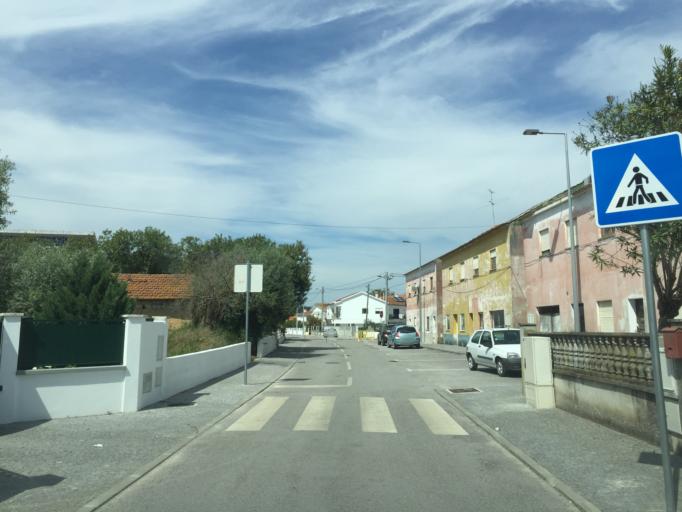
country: PT
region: Coimbra
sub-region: Soure
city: Soure
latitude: 40.0054
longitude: -8.5813
